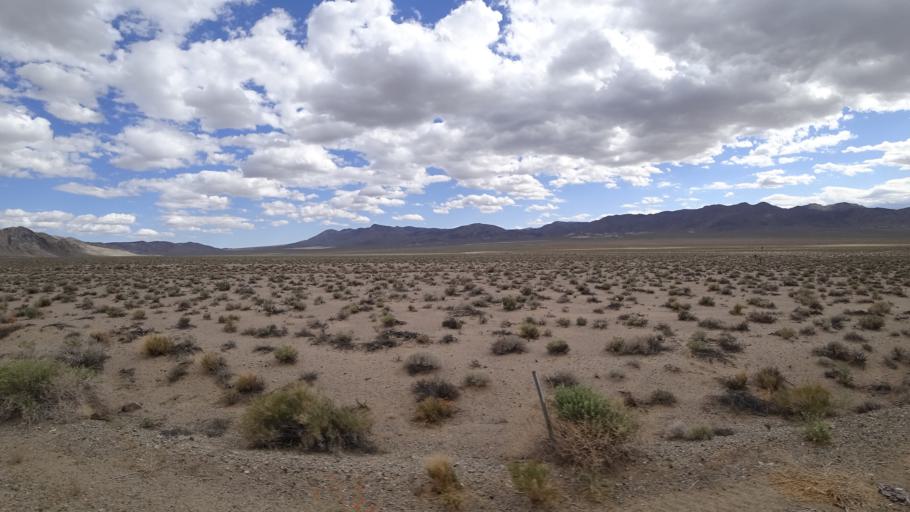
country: US
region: California
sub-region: Inyo County
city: Lone Pine
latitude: 36.3330
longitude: -117.7328
